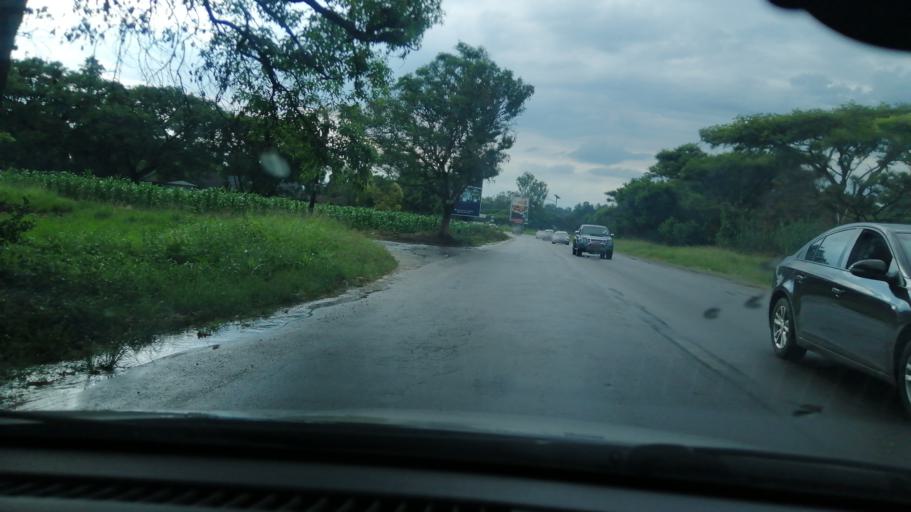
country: ZW
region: Harare
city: Harare
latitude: -17.7896
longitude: 31.0549
